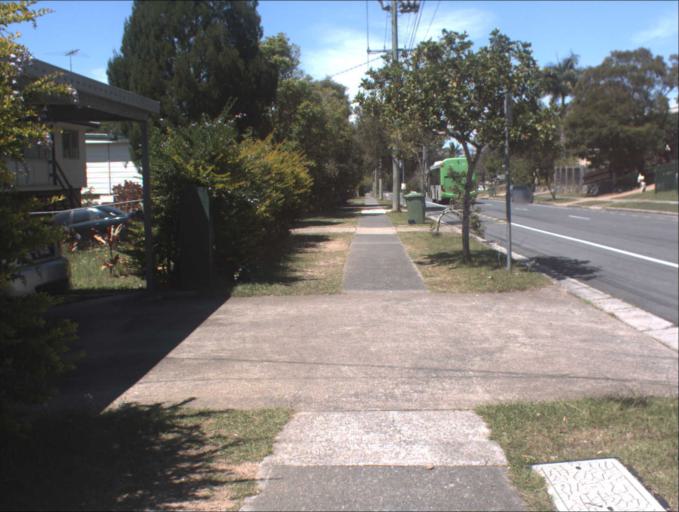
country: AU
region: Queensland
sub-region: Logan
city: Logan City
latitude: -27.6612
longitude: 153.1086
